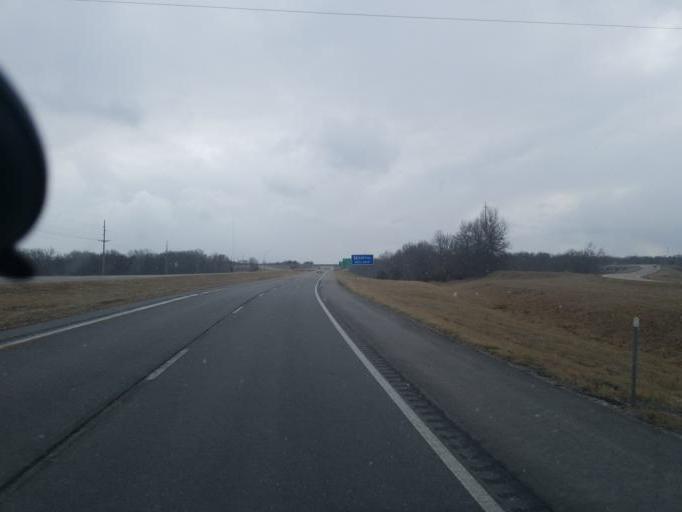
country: US
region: Missouri
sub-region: Randolph County
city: Moberly
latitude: 39.4241
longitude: -92.4120
